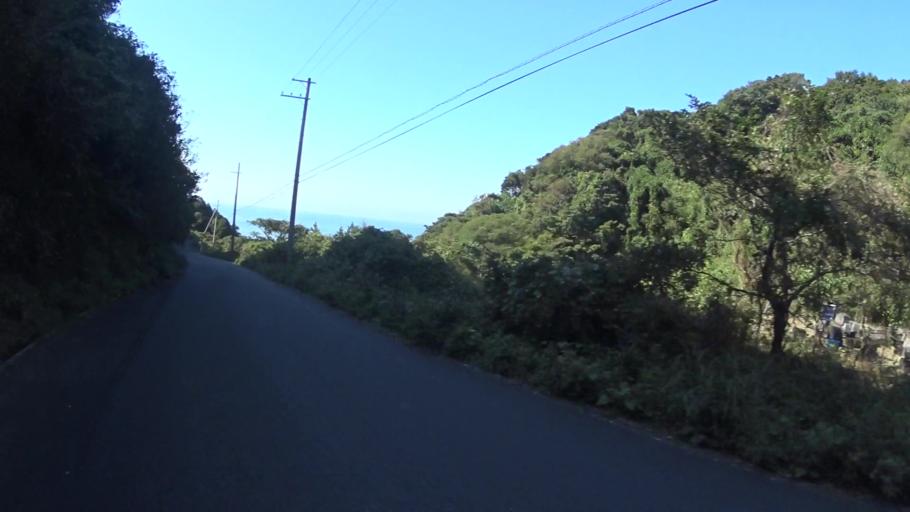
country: JP
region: Kyoto
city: Miyazu
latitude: 35.7711
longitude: 135.2231
